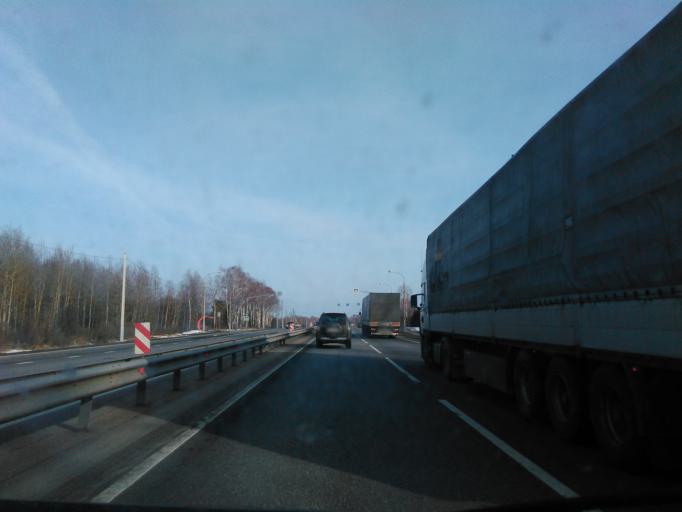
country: RU
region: Smolensk
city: Verkhnedneprovskiy
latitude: 55.1819
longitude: 33.5605
